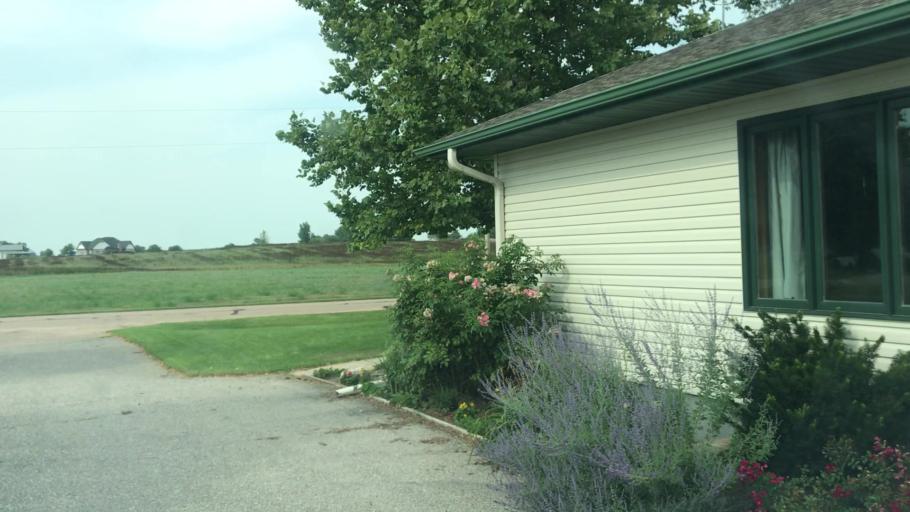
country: US
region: Nebraska
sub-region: Hall County
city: Wood River
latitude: 41.0061
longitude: -98.6059
